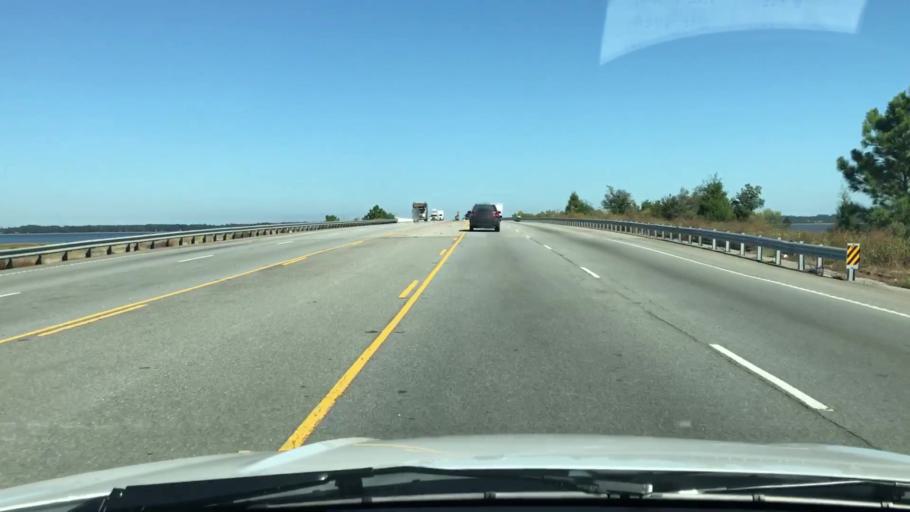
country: US
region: South Carolina
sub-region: Beaufort County
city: Shell Point
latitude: 32.3758
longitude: -80.7965
